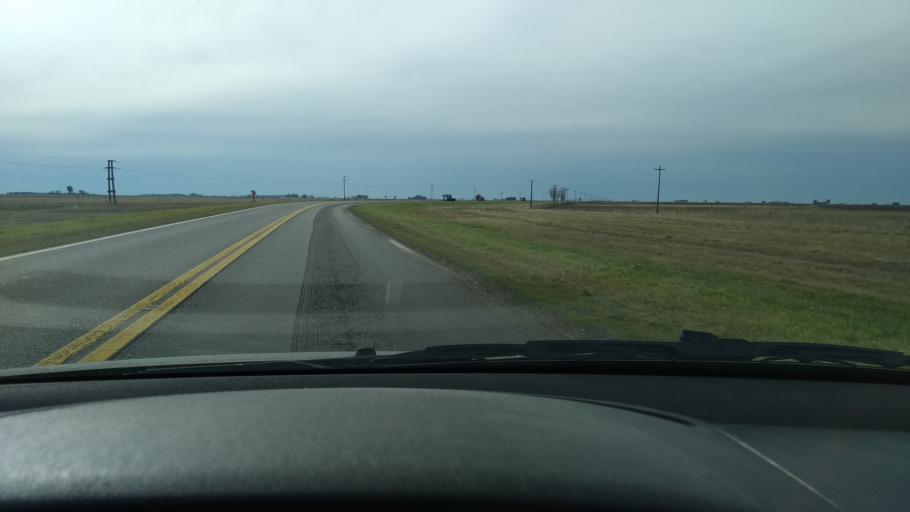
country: AR
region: Buenos Aires
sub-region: Partido de Azul
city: Azul
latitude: -36.7096
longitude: -59.7599
